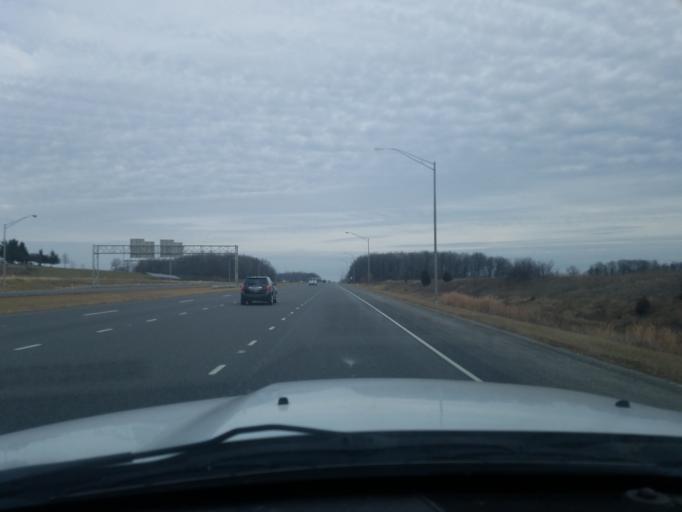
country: US
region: Indiana
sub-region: Huntington County
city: Roanoke
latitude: 40.9665
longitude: -85.2869
